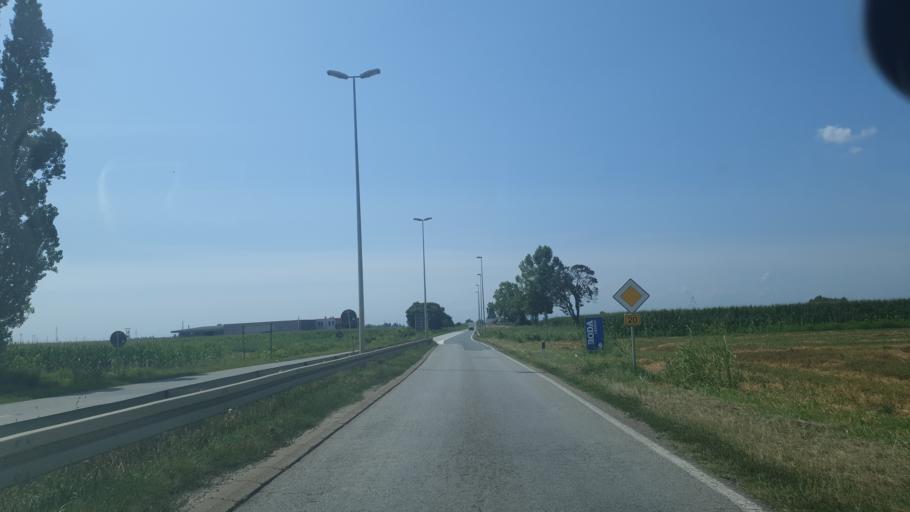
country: RS
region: Autonomna Pokrajina Vojvodina
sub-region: Sremski Okrug
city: Sremska Mitrovica
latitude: 44.9946
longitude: 19.6413
